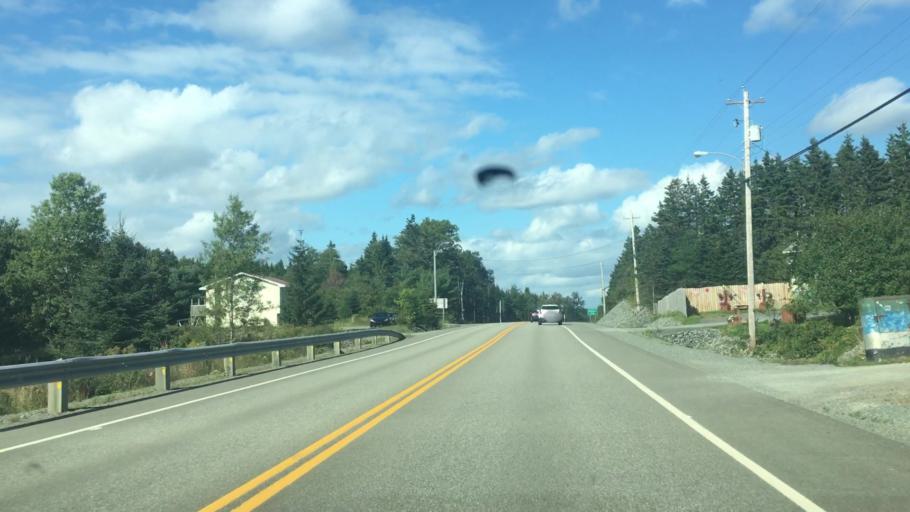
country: CA
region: Nova Scotia
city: Princeville
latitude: 45.6883
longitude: -60.7531
